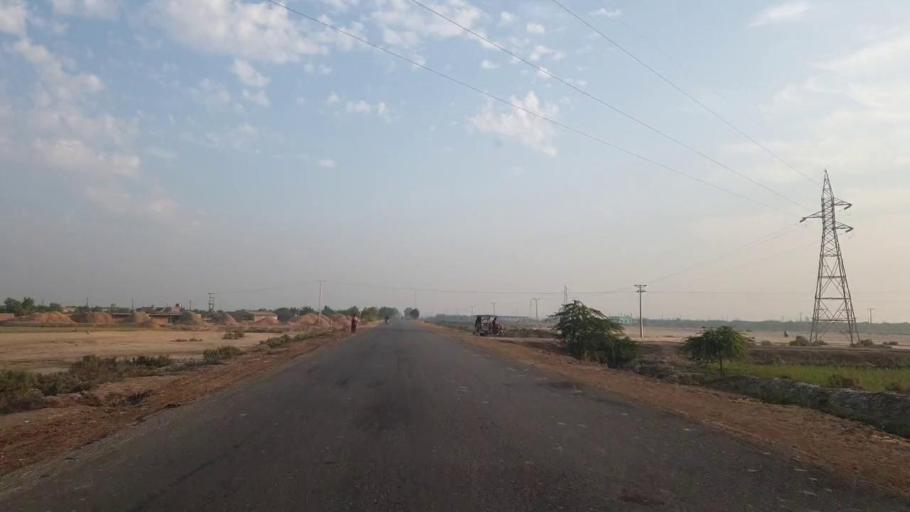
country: PK
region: Sindh
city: Badin
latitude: 24.6868
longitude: 68.9139
